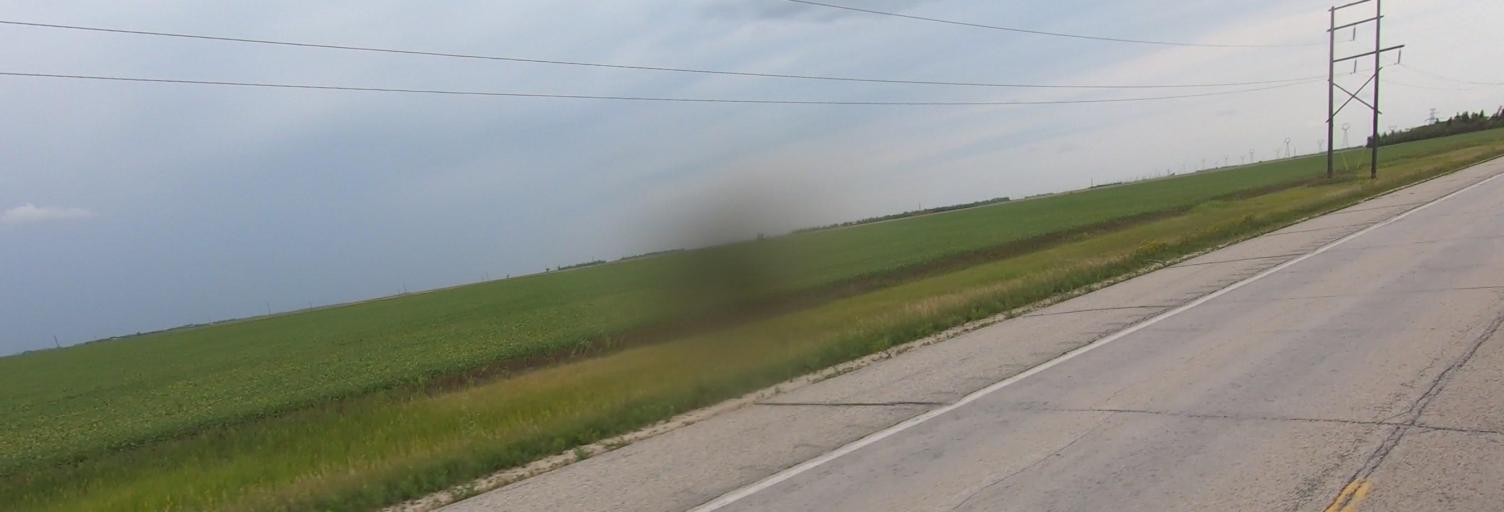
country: CA
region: Manitoba
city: Headingley
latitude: 49.7337
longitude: -97.3635
